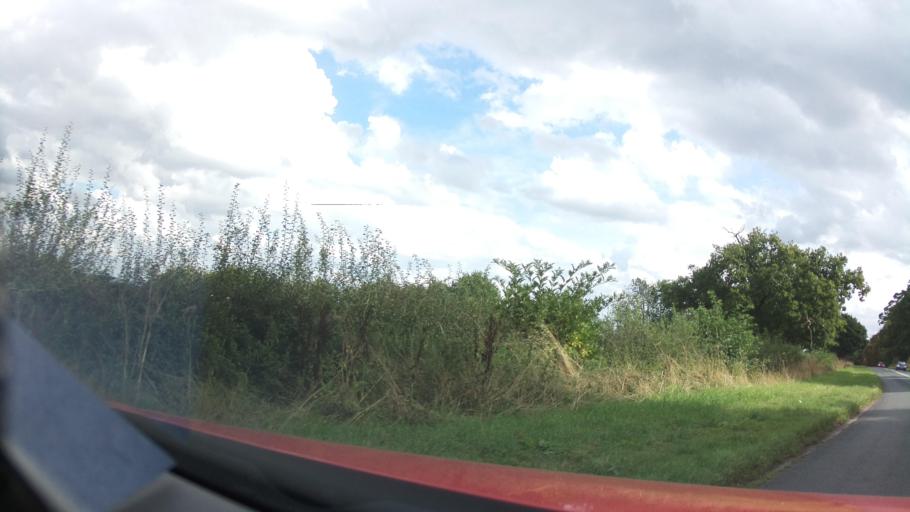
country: GB
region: England
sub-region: North Yorkshire
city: Bedale
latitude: 54.1998
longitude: -1.5825
